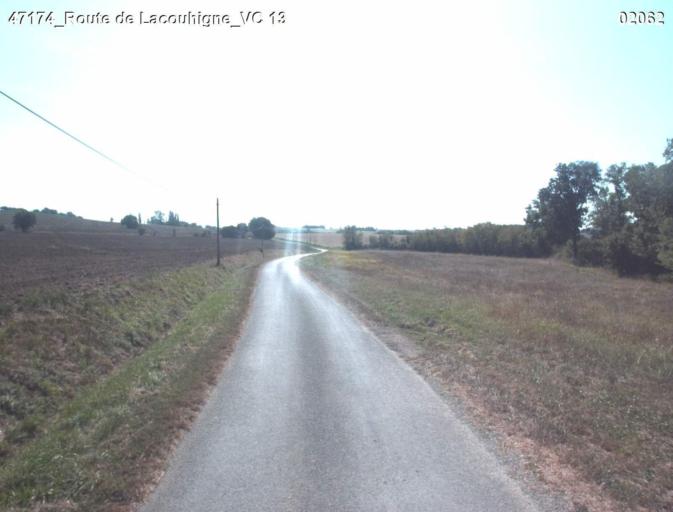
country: FR
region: Midi-Pyrenees
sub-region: Departement du Gers
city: Condom
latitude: 44.0291
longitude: 0.3730
